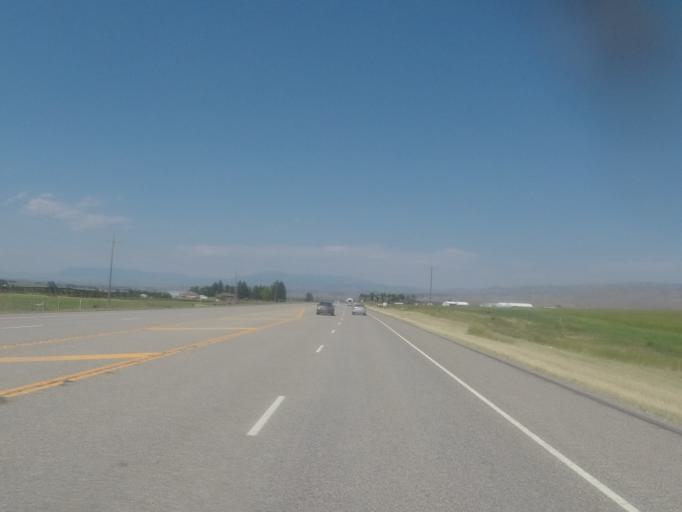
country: US
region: Montana
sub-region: Broadwater County
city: Townsend
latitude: 46.1329
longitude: -111.4848
